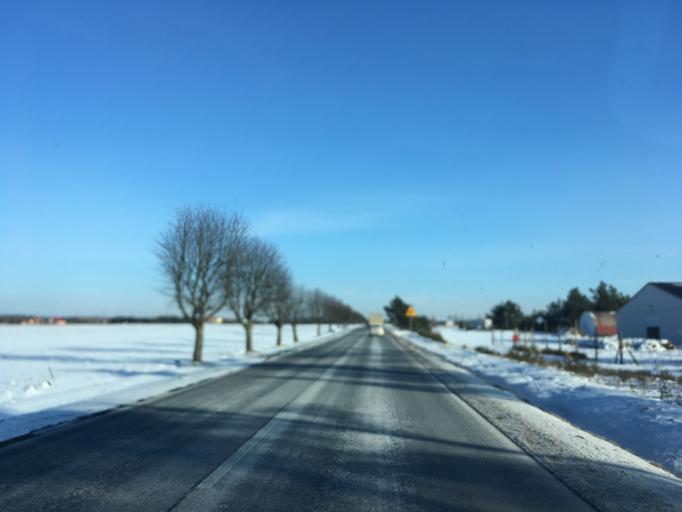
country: PL
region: Pomeranian Voivodeship
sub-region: Powiat koscierski
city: Lipusz
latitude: 54.1326
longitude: 17.8446
